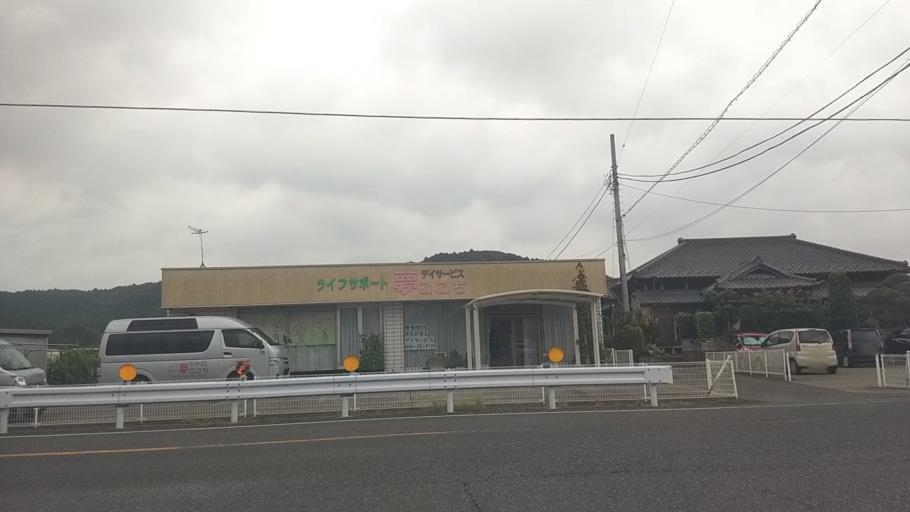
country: JP
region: Chiba
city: Kisarazu
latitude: 35.3119
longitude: 140.0626
